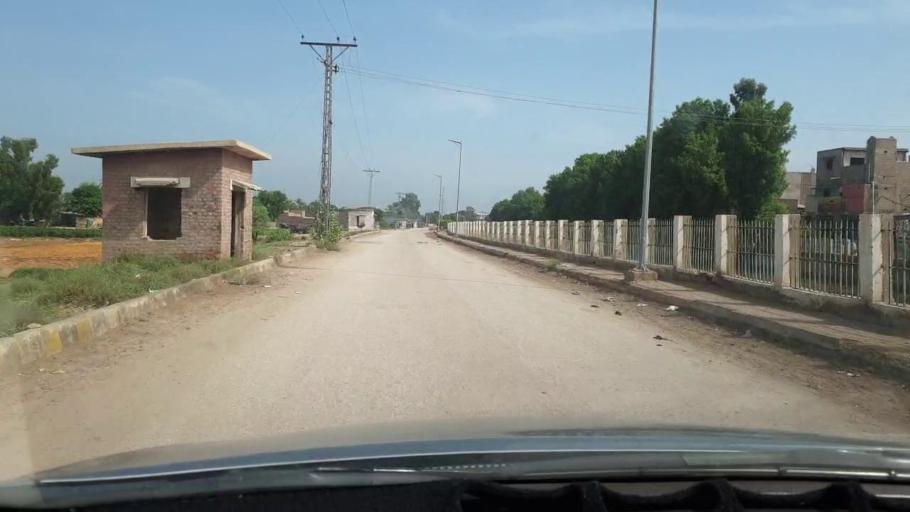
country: PK
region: Sindh
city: Khairpur
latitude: 27.5272
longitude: 68.7539
